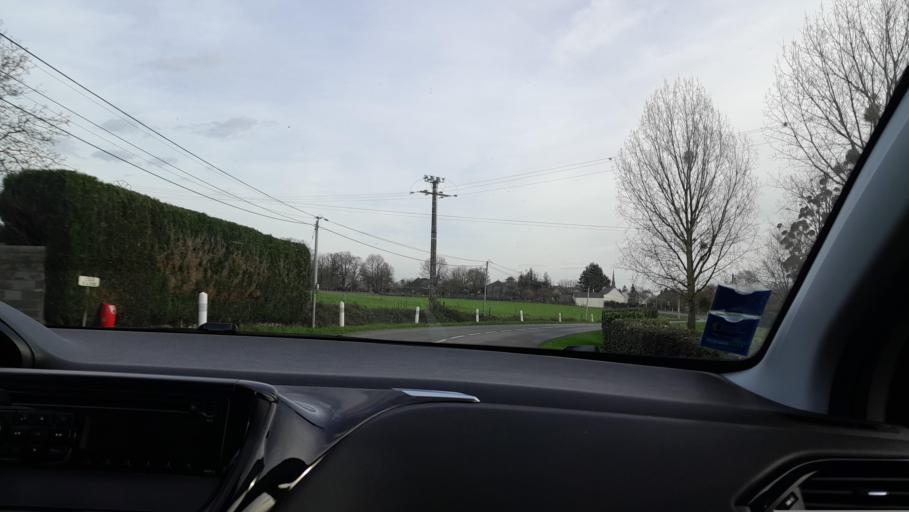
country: FR
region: Brittany
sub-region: Departement d'Ille-et-Vilaine
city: Argentre-du-Plessis
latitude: 47.9687
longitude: -1.1310
